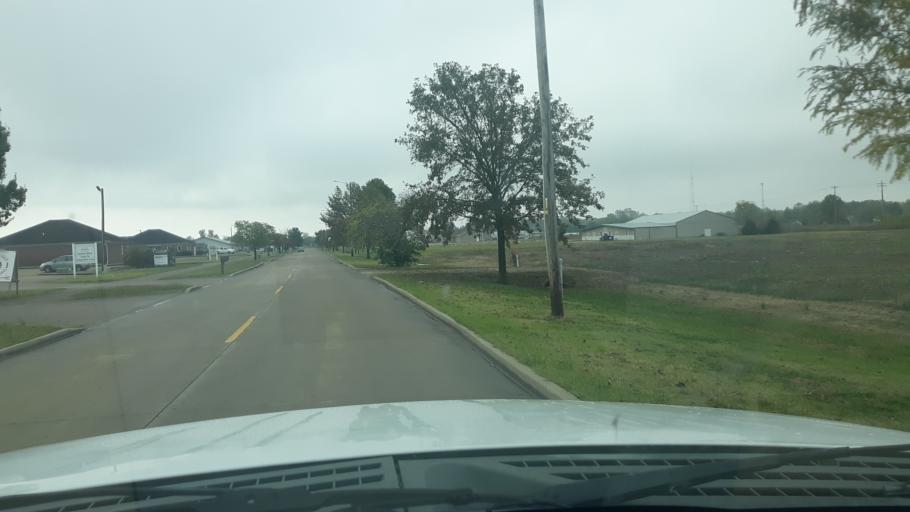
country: US
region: Illinois
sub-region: Saline County
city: Harrisburg
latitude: 37.7486
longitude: -88.5306
